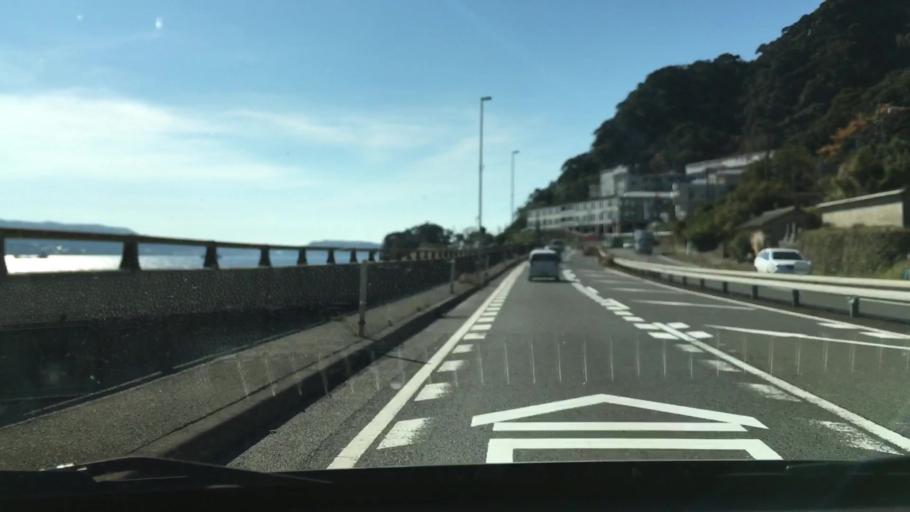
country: JP
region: Kagoshima
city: Kagoshima-shi
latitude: 31.6359
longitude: 130.6022
